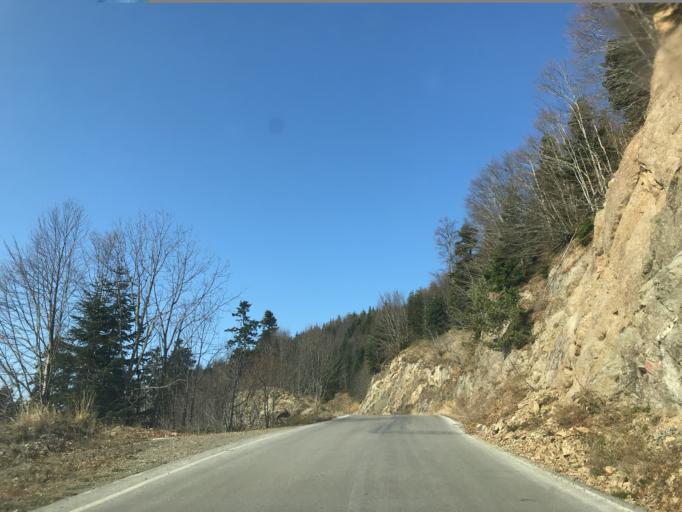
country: TR
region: Bolu
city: Bolu
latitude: 40.8853
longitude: 31.6825
